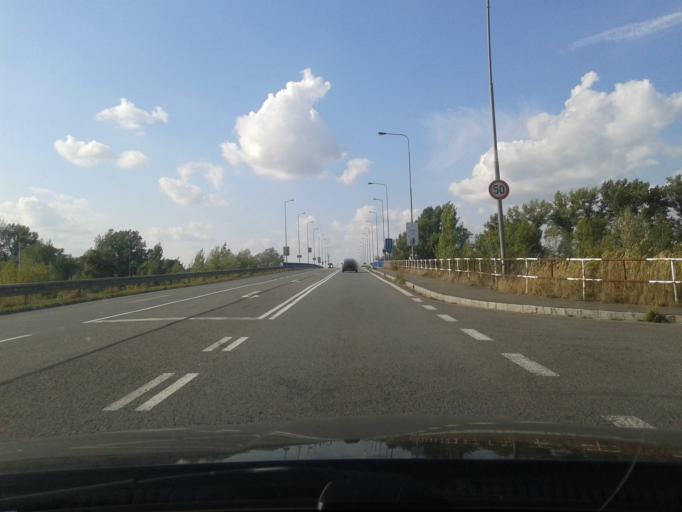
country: CZ
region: Moravskoslezsky
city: Stary Bohumin
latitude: 49.9152
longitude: 18.3255
